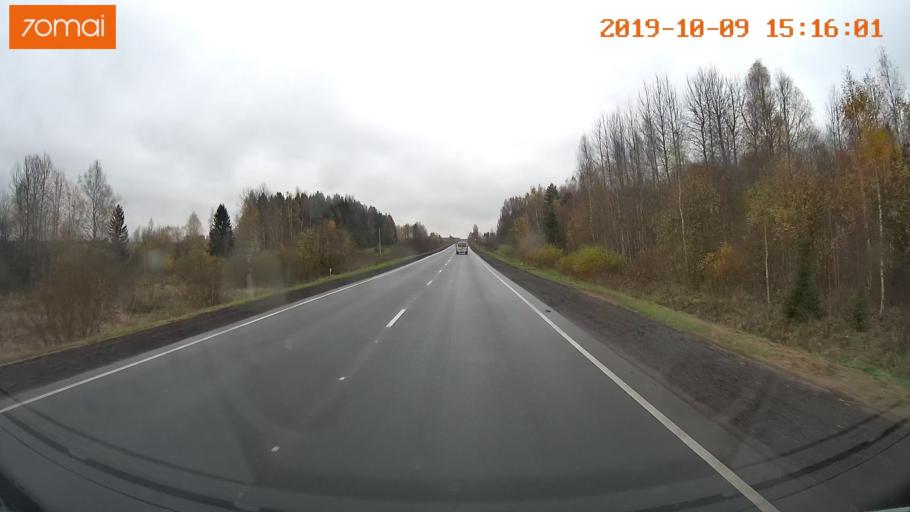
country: RU
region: Kostroma
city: Susanino
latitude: 58.1151
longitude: 41.5874
